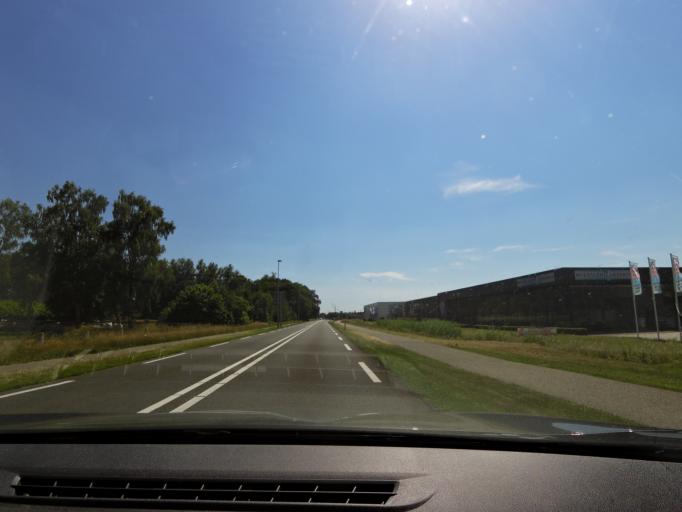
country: NL
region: Gelderland
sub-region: Berkelland
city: Eibergen
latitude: 52.0592
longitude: 6.6285
